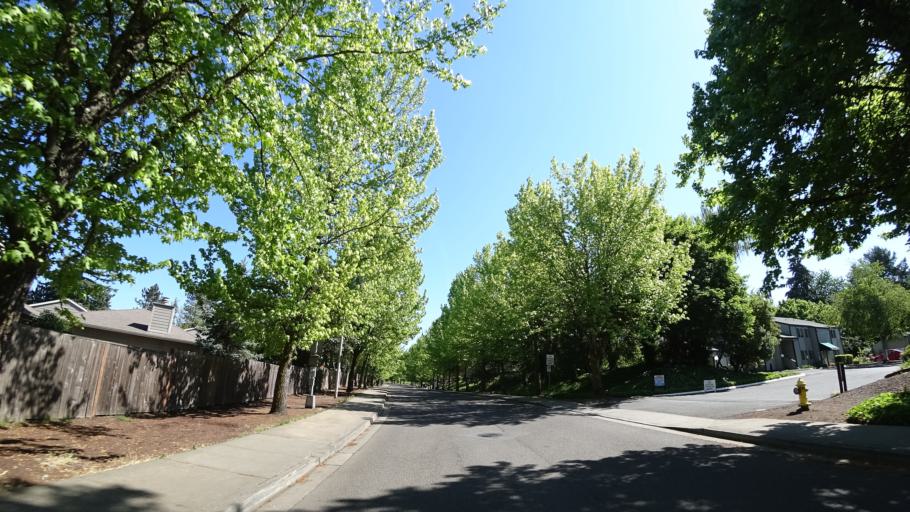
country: US
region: Oregon
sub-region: Washington County
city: Beaverton
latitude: 45.4526
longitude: -122.8031
